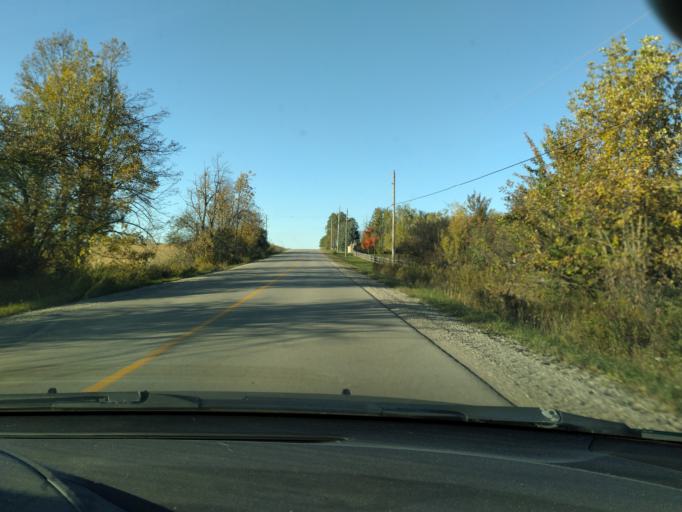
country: CA
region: Ontario
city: Bradford West Gwillimbury
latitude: 44.0337
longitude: -79.7298
